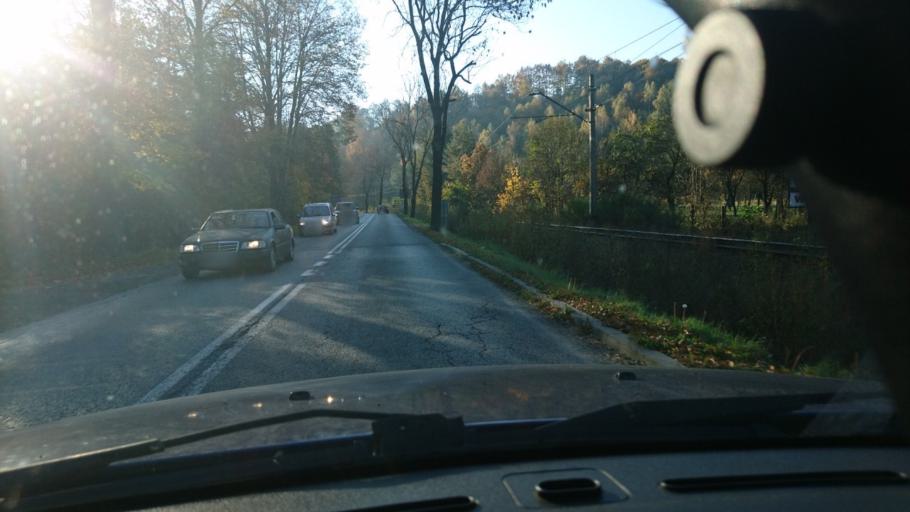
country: PL
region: Silesian Voivodeship
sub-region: Powiat cieszynski
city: Wisla
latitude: 49.6832
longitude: 18.8396
